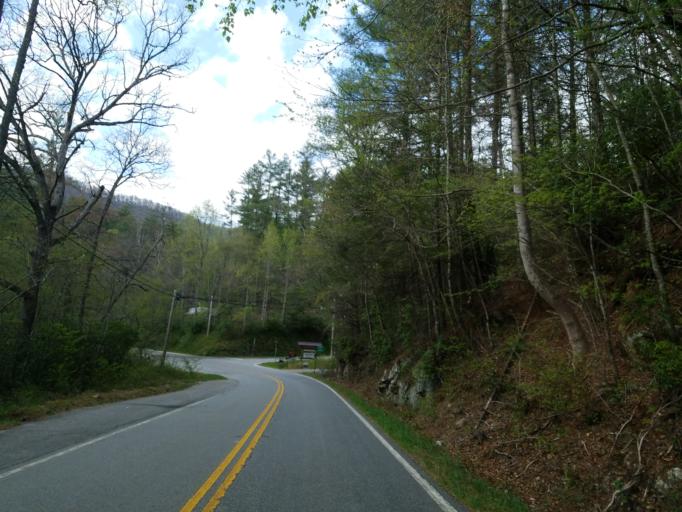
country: US
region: Georgia
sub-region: Union County
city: Blairsville
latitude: 34.7373
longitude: -84.0796
